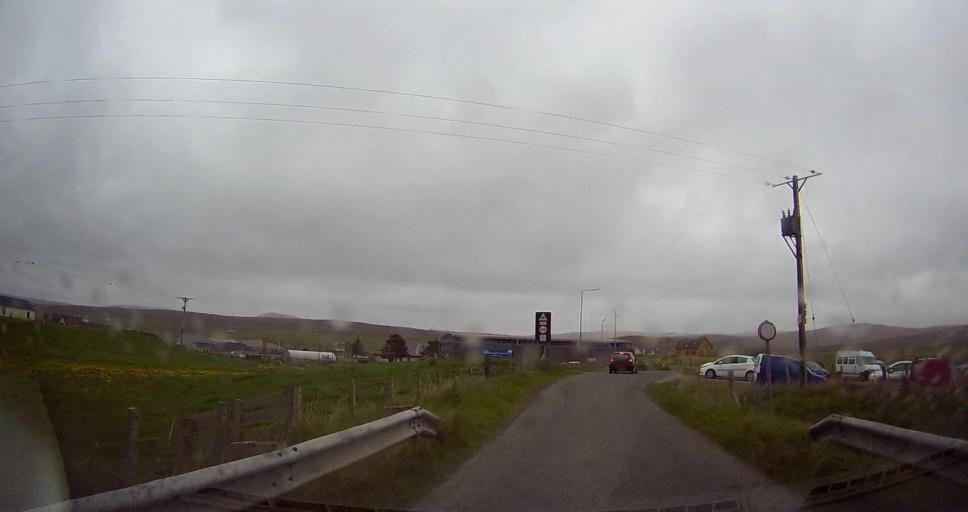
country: GB
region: Scotland
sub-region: Shetland Islands
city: Lerwick
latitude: 60.2840
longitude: -1.3817
